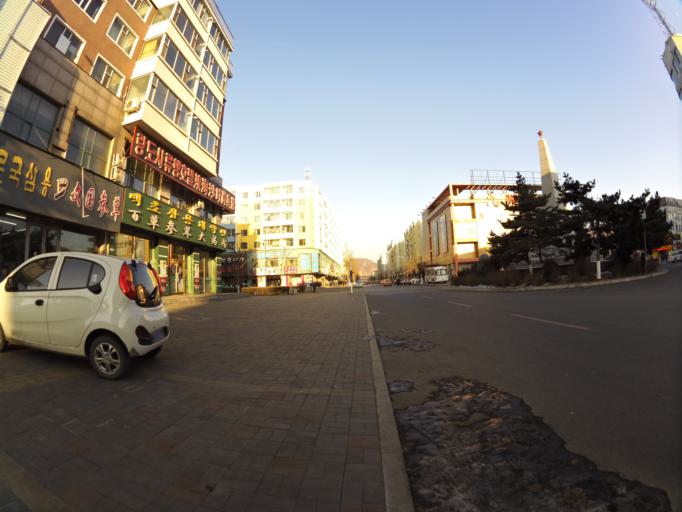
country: CN
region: Jilin Sheng
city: Tumen
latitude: 42.9629
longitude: 129.8388
